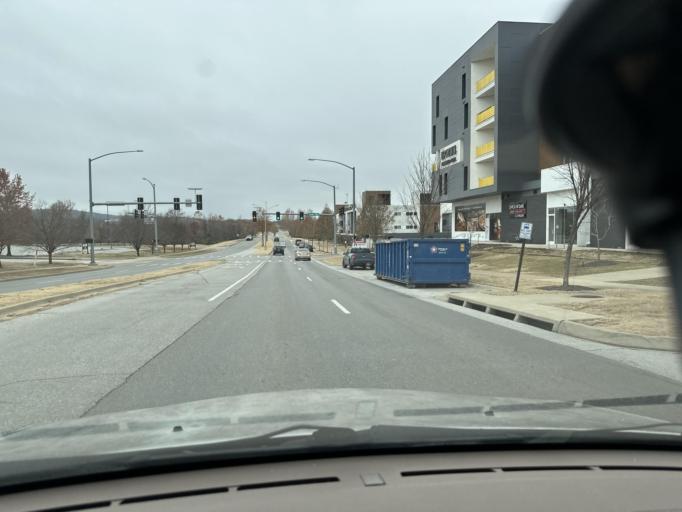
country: US
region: Arkansas
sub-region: Washington County
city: Johnson
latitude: 36.1235
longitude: -94.1567
